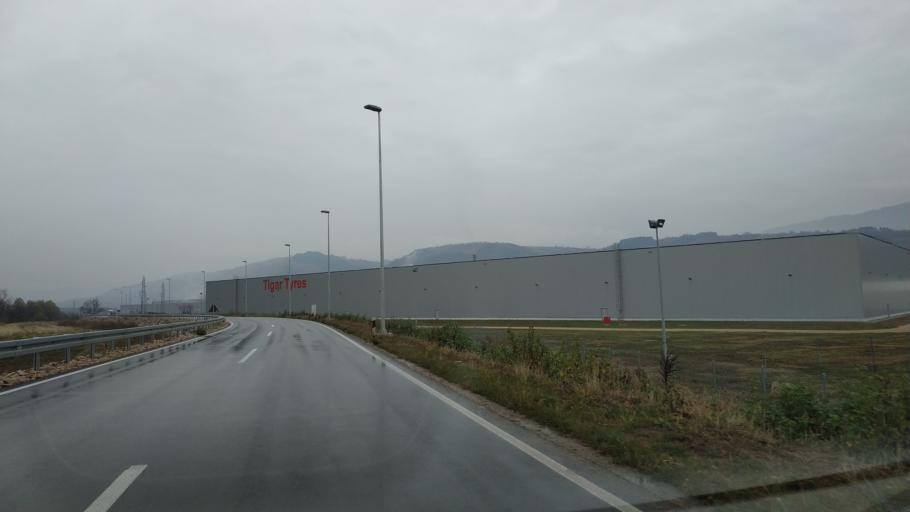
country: RS
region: Central Serbia
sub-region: Pirotski Okrug
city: Pirot
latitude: 43.1669
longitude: 22.5759
